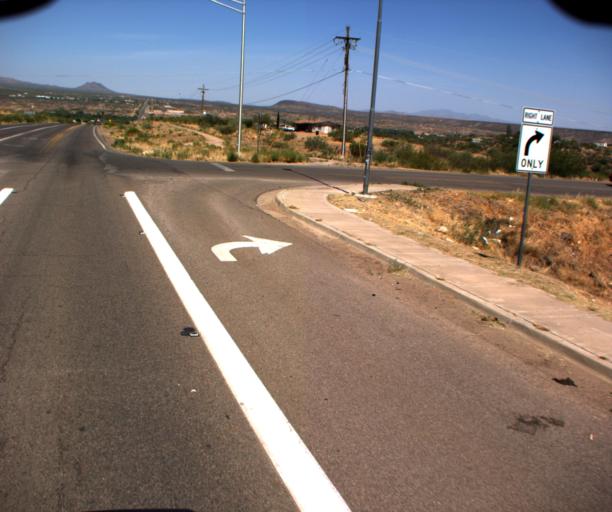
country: US
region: Arizona
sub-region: Gila County
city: Peridot
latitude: 33.2931
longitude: -110.4374
